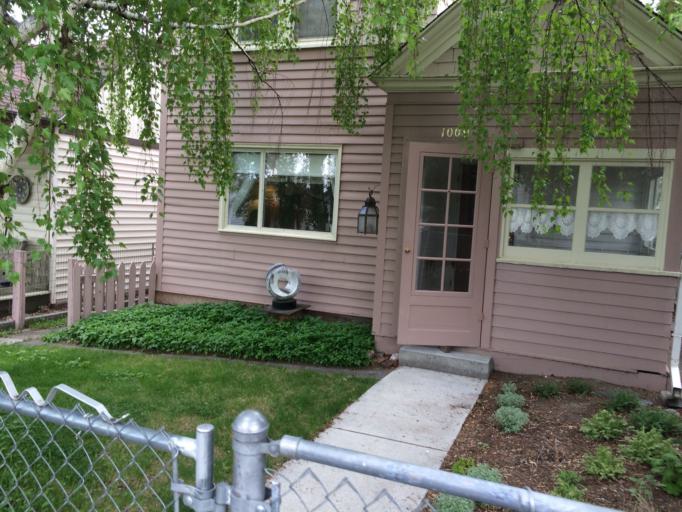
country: US
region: Montana
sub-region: Lewis and Clark County
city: Helena
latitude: 46.5887
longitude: -112.0234
